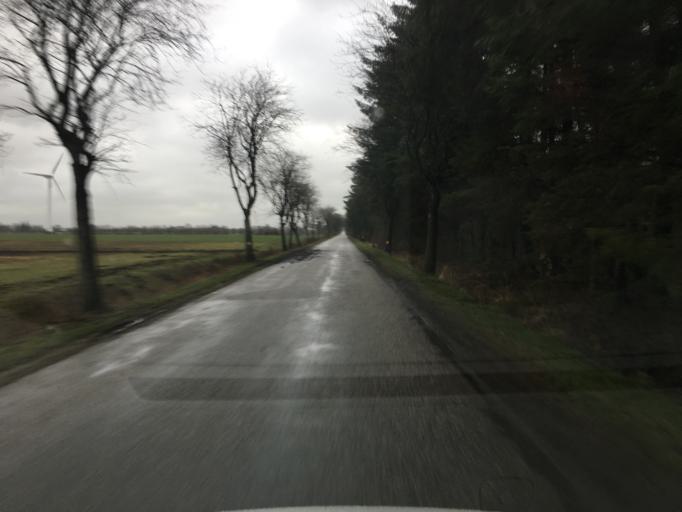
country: DK
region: South Denmark
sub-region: Aabenraa Kommune
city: Krusa
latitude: 54.8998
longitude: 9.3485
